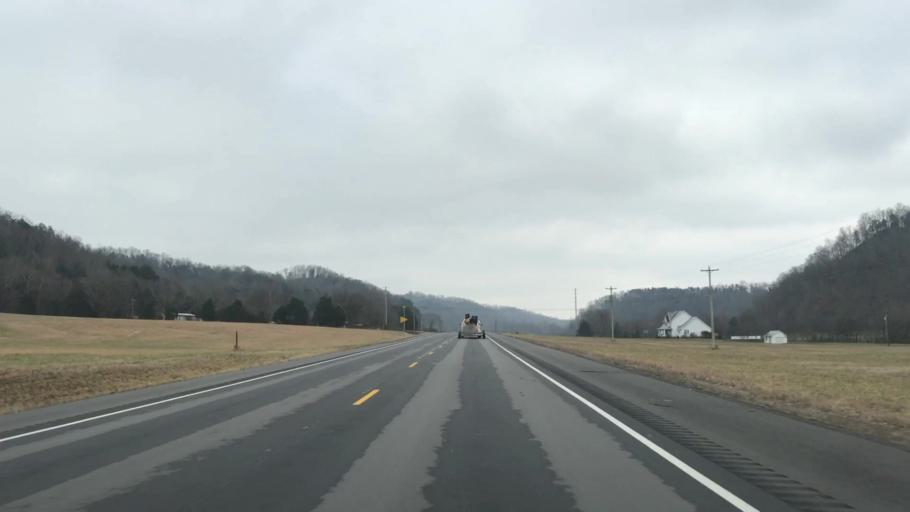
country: US
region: Kentucky
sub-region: Cumberland County
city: Burkesville
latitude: 36.8436
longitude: -85.3711
